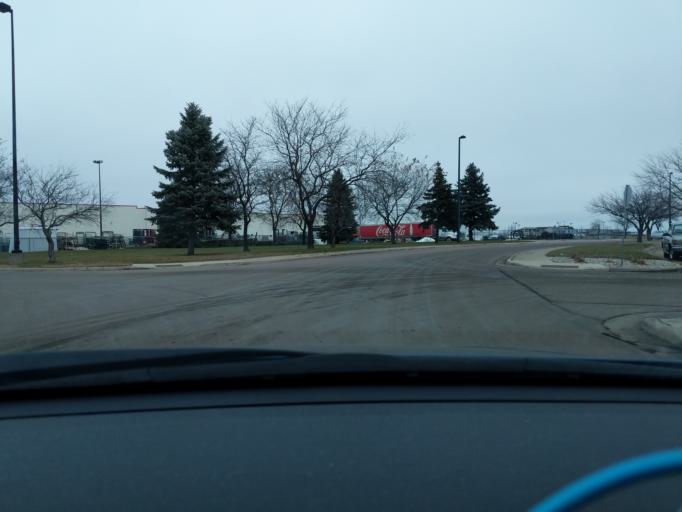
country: US
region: Minnesota
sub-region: Lyon County
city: Marshall
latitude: 44.4355
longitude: -95.7705
